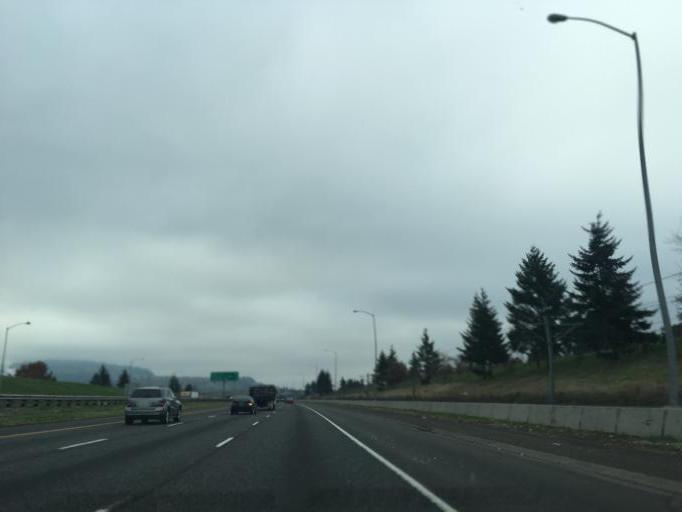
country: US
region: Oregon
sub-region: Multnomah County
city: Lents
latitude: 45.4891
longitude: -122.5662
